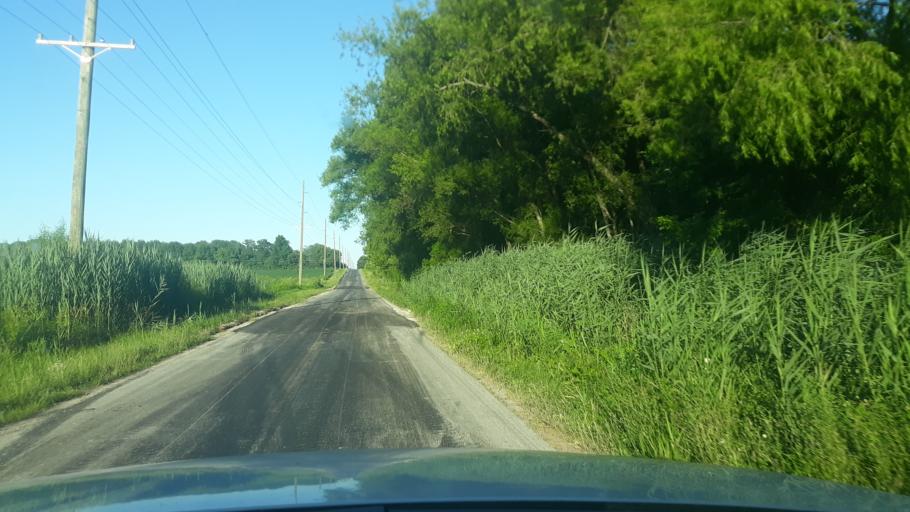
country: US
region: Illinois
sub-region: Saline County
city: Harrisburg
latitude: 37.8631
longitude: -88.5752
